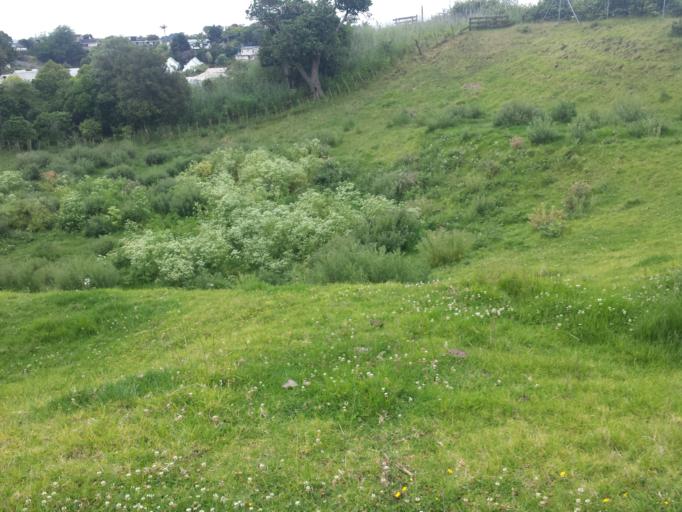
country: NZ
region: Auckland
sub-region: Auckland
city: Tamaki
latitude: -36.8646
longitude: 174.8711
